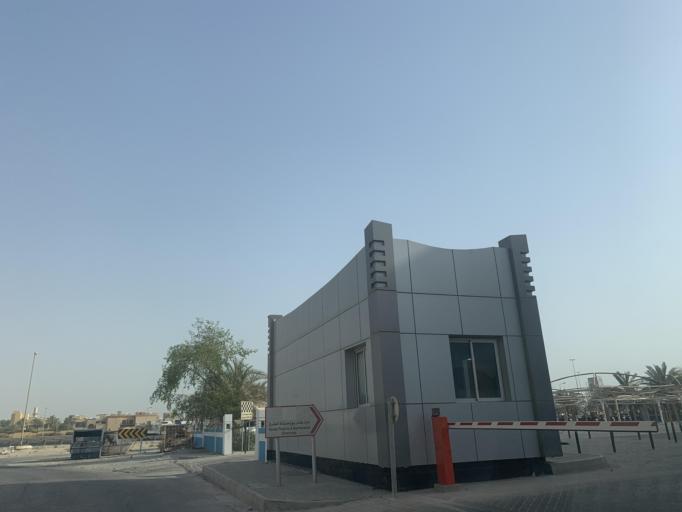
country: BH
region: Central Governorate
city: Madinat Hamad
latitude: 26.1738
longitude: 50.4697
